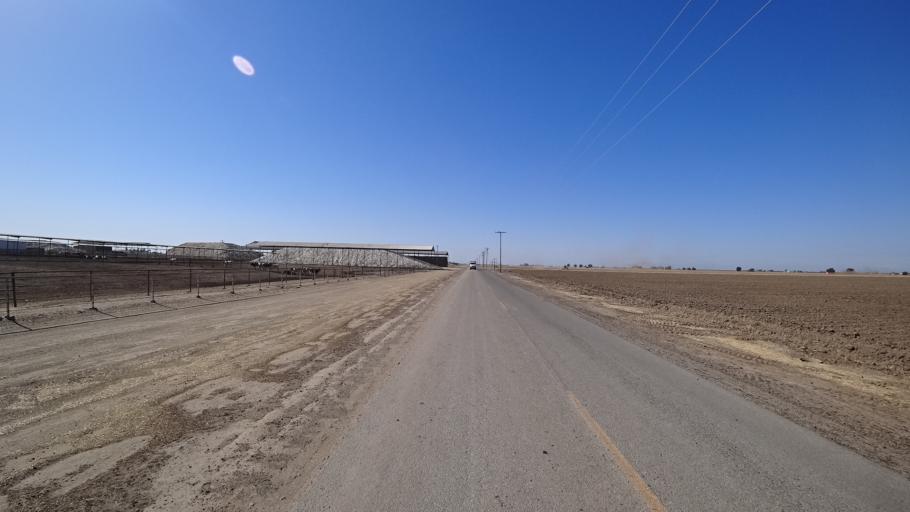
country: US
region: California
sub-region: Kings County
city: Home Garden
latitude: 36.2422
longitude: -119.5562
